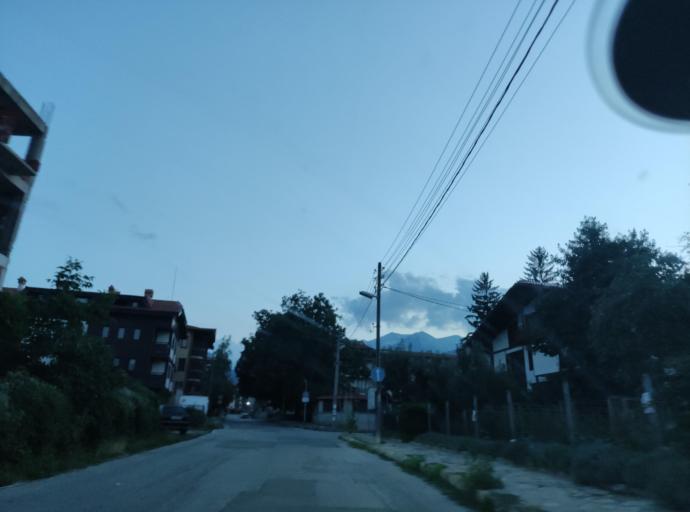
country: BG
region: Blagoevgrad
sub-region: Obshtina Bansko
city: Bansko
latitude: 41.8298
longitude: 23.4845
